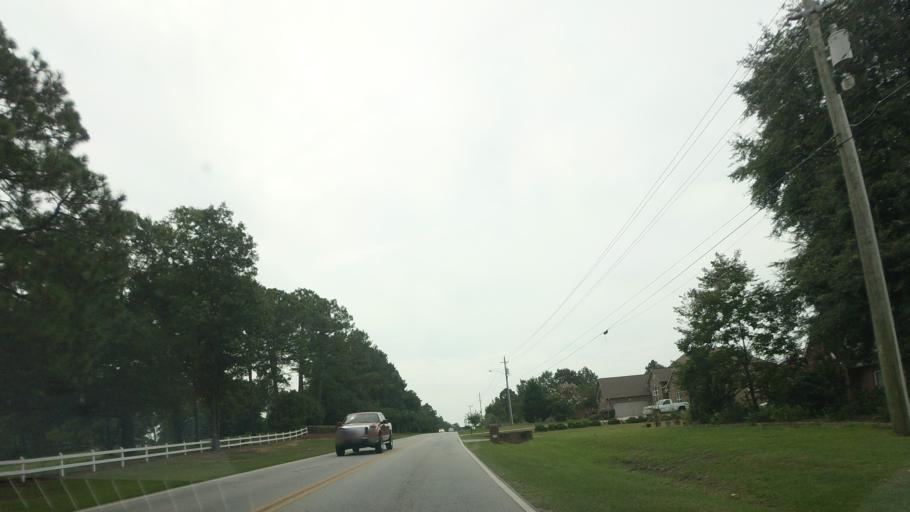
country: US
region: Georgia
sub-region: Houston County
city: Robins Air Force Base
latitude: 32.5725
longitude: -83.5893
